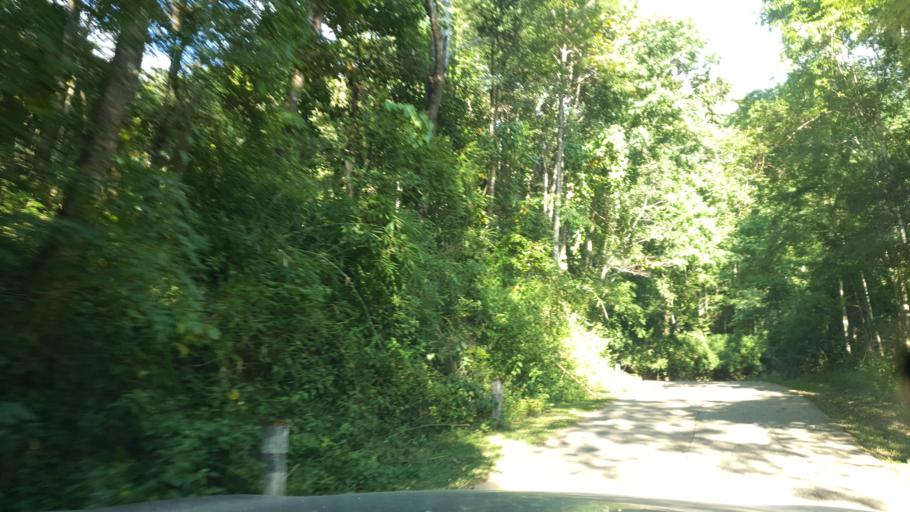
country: TH
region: Chiang Mai
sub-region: Amphoe Chiang Dao
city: Chiang Dao
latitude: 19.3833
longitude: 98.7727
